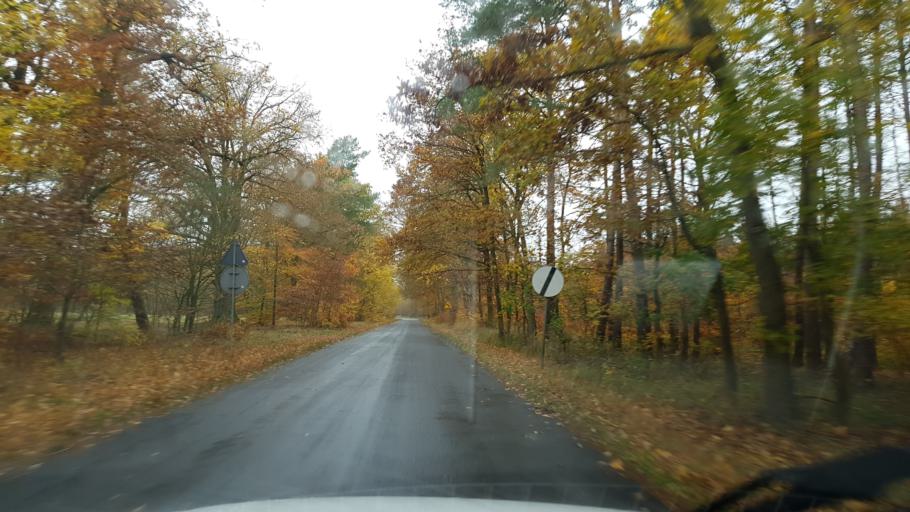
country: PL
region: West Pomeranian Voivodeship
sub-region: Powiat goleniowski
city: Stepnica
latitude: 53.6552
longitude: 14.6695
